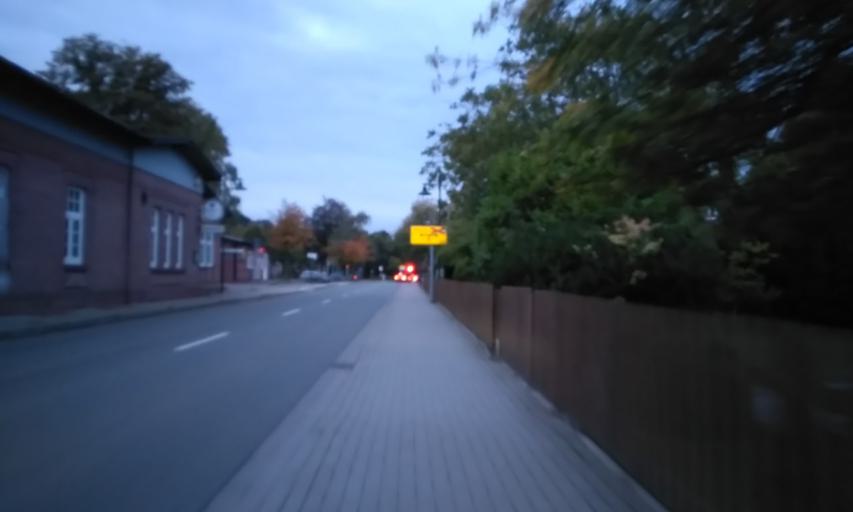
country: DE
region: Lower Saxony
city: Harsefeld
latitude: 53.4503
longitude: 9.4991
